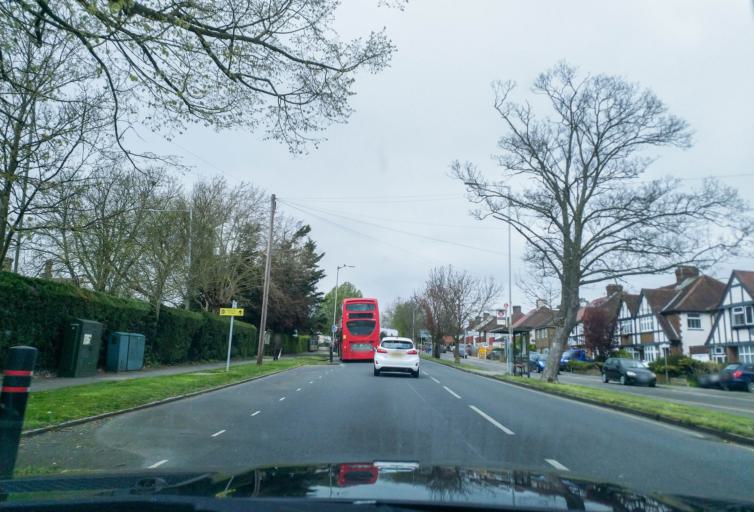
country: GB
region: England
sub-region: Greater London
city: Pinner
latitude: 51.5725
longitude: -0.3936
